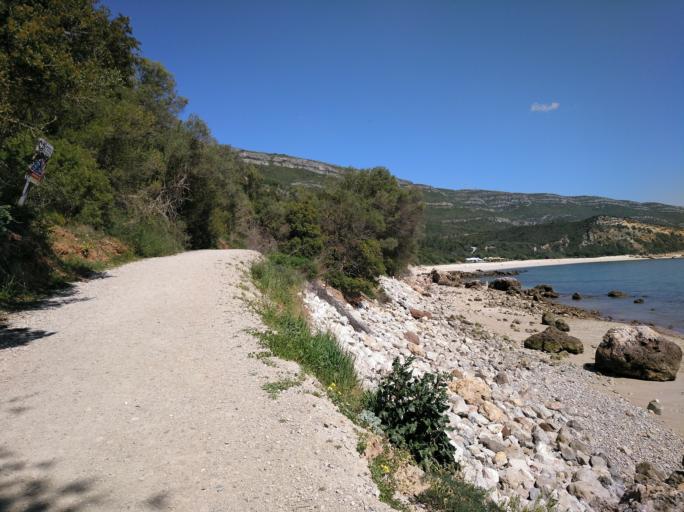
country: PT
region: Setubal
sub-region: Palmela
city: Quinta do Anjo
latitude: 38.4767
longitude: -8.9842
